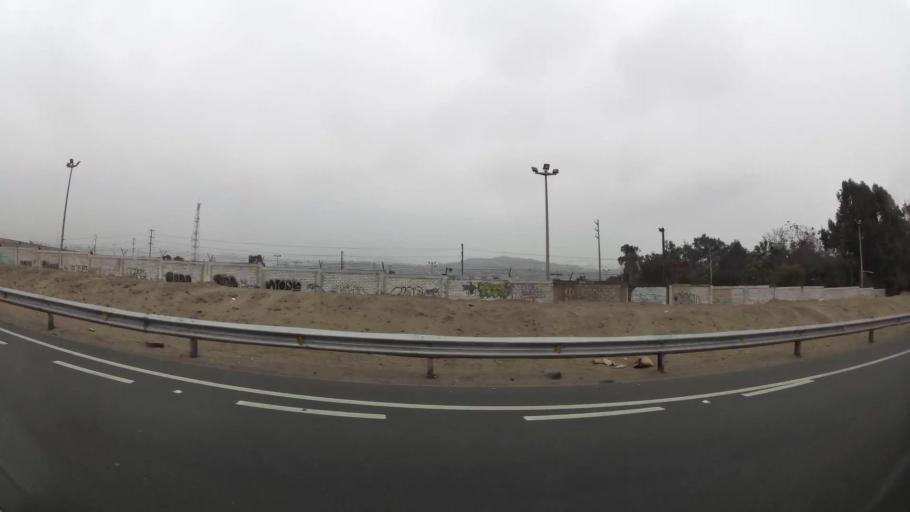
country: PE
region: Lima
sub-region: Lima
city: Surco
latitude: -12.1805
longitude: -76.9760
